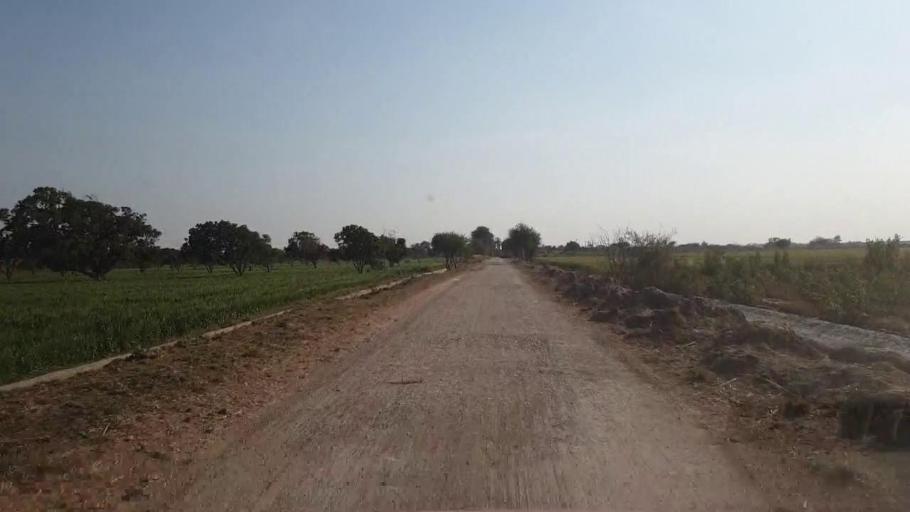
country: PK
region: Sindh
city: Chambar
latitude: 25.3501
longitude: 68.7338
